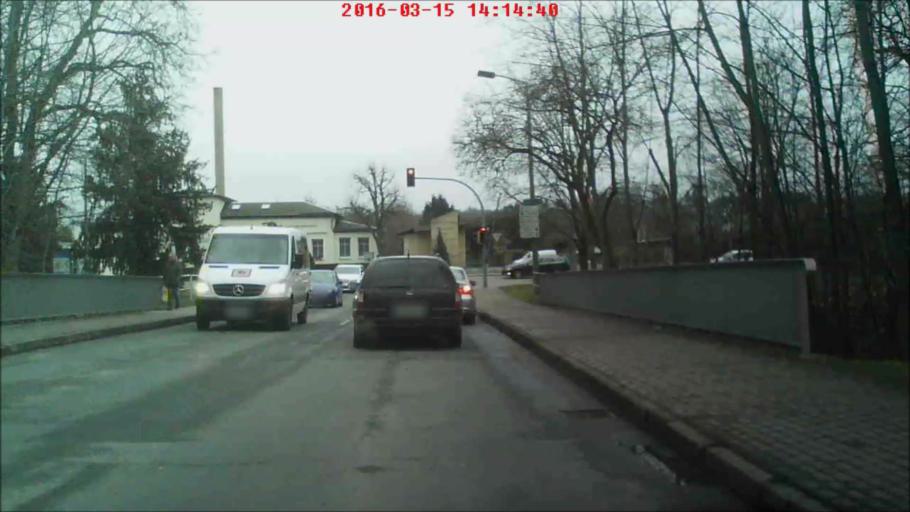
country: DE
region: Thuringia
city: Arnstadt
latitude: 50.8386
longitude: 10.9575
